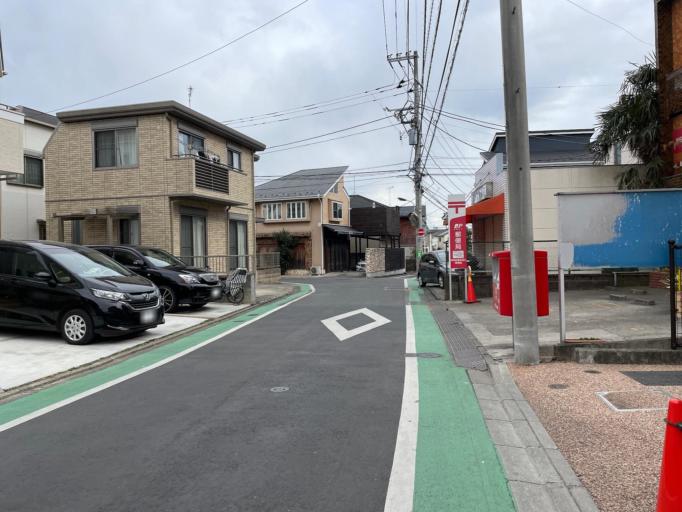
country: JP
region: Tokyo
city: Chofugaoka
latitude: 35.6274
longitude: 139.5998
